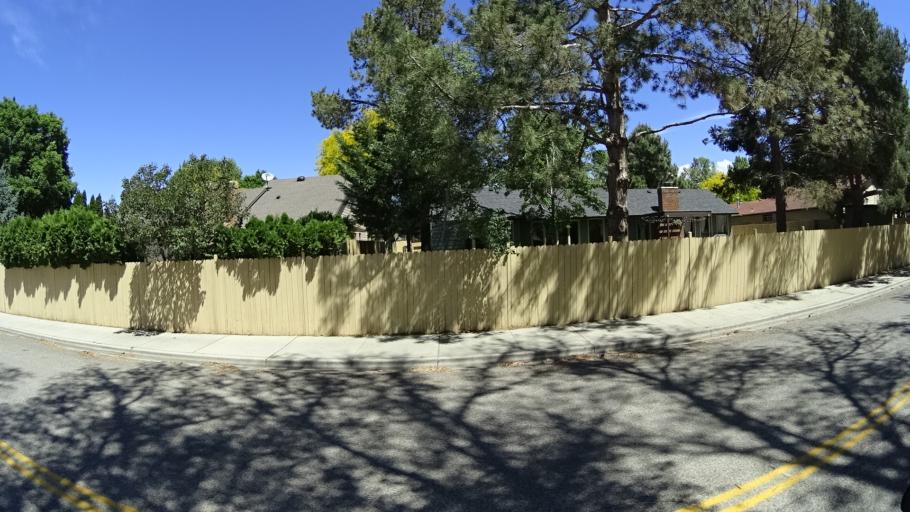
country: US
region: Idaho
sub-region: Ada County
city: Boise
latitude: 43.5678
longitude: -116.1560
